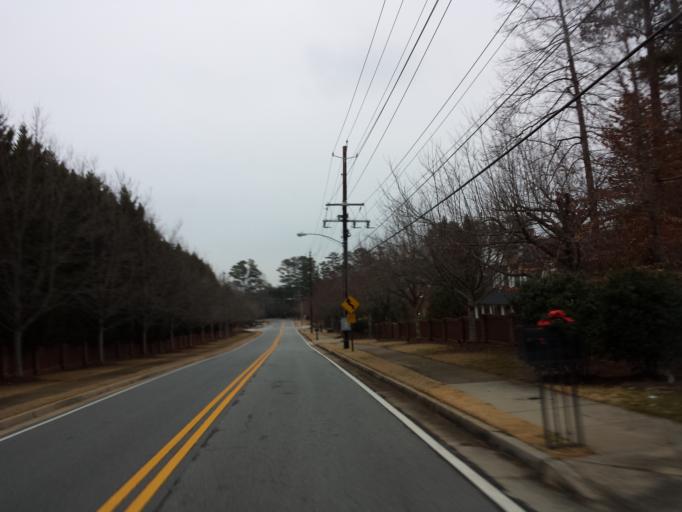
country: US
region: Georgia
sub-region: Fulton County
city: Sandy Springs
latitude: 33.9532
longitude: -84.4229
